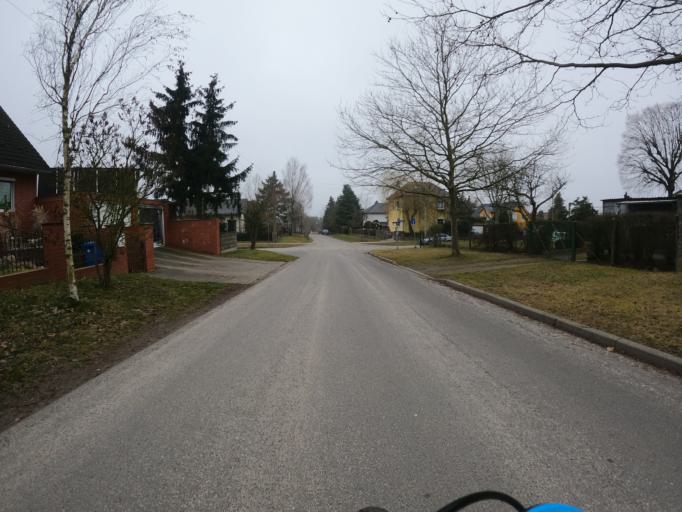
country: DE
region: Brandenburg
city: Hoppegarten
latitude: 52.5297
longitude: 13.6610
